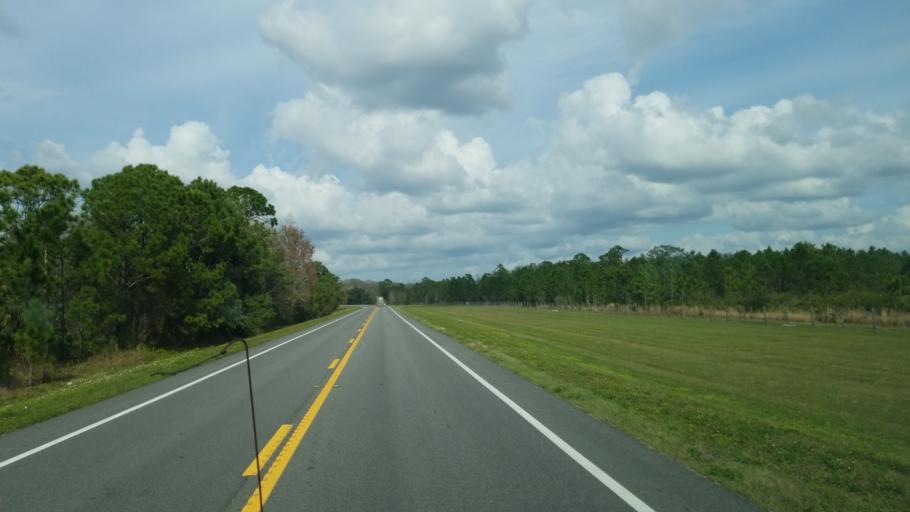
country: US
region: Florida
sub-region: Indian River County
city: Fellsmere
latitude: 27.7451
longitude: -80.9033
